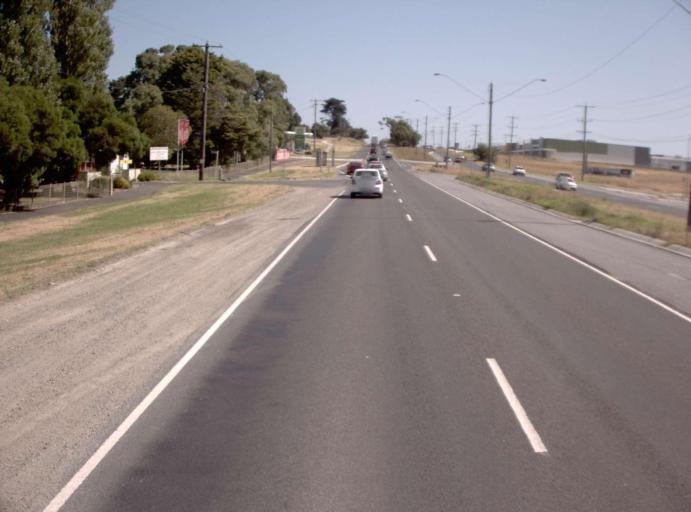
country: AU
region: Victoria
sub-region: Frankston
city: Carrum Downs
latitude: -38.0946
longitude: 145.1768
